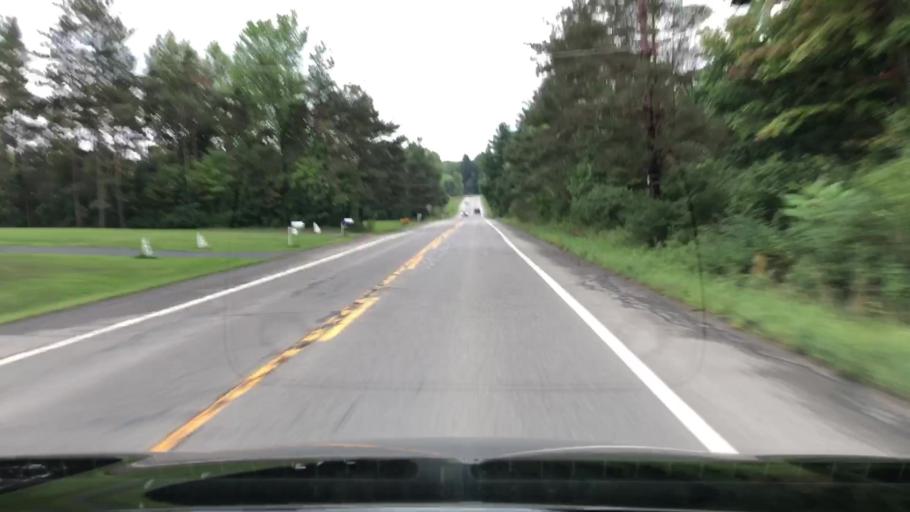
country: US
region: New York
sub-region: Erie County
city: Orchard Park
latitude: 42.7580
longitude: -78.6969
